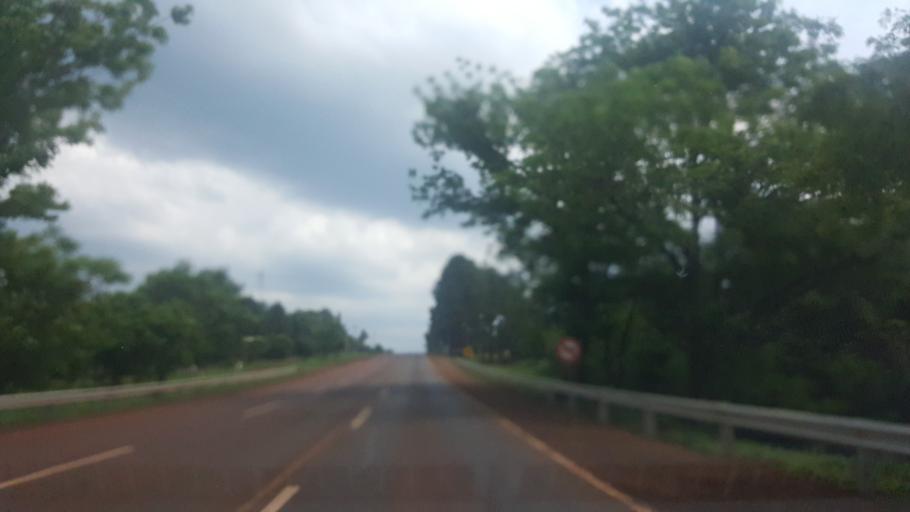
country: AR
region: Misiones
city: Jardin America
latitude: -27.0818
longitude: -55.2847
